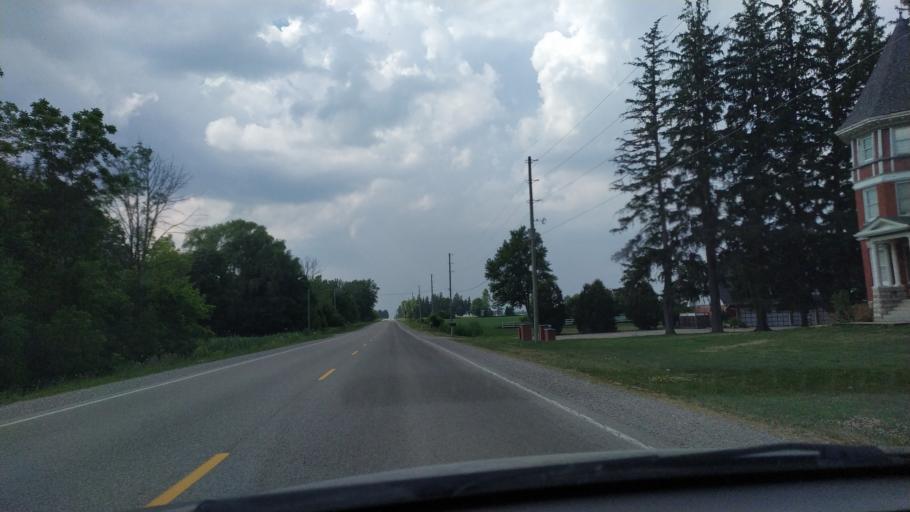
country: CA
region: Ontario
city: London
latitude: 43.1120
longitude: -81.1621
